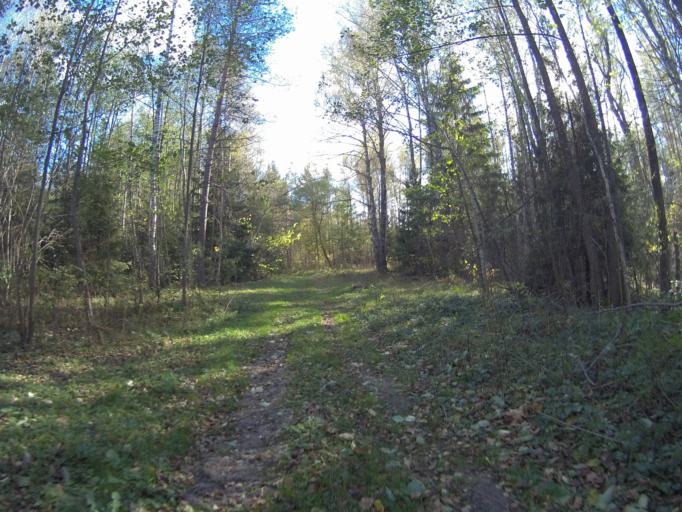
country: RU
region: Vladimir
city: Golovino
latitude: 56.0124
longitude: 40.4826
